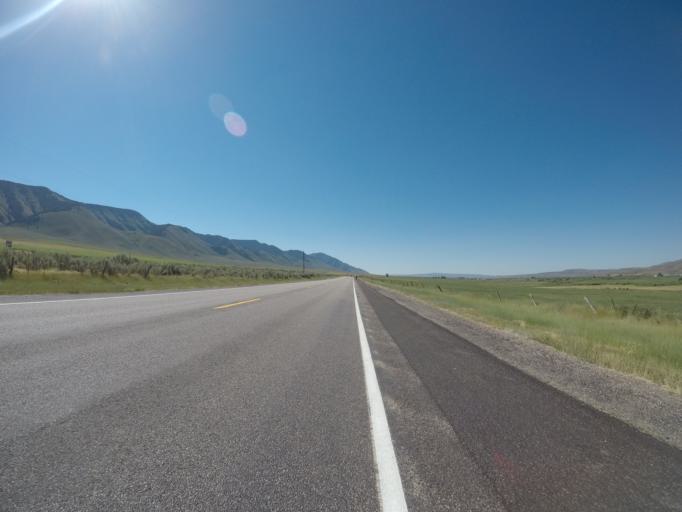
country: US
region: Idaho
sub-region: Bear Lake County
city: Montpelier
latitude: 42.3547
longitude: -111.0485
